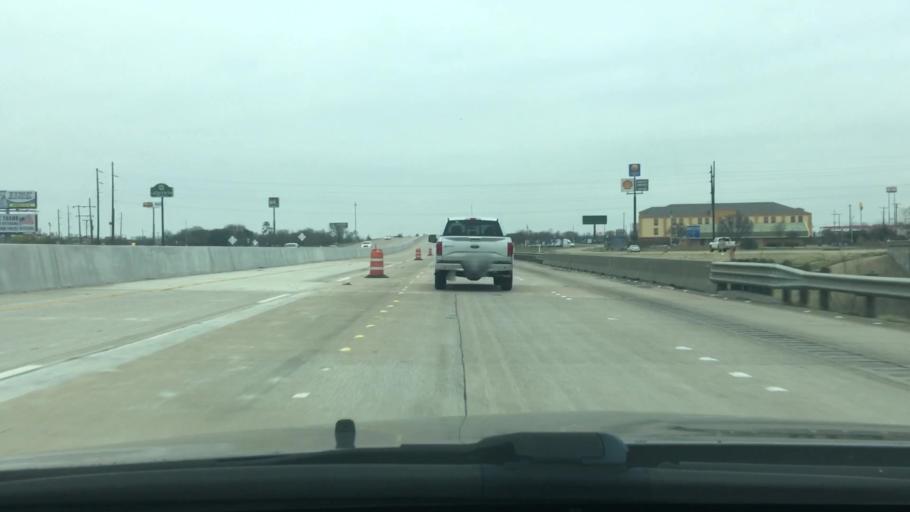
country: US
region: Texas
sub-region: Navarro County
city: Corsicana
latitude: 32.1020
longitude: -96.4421
